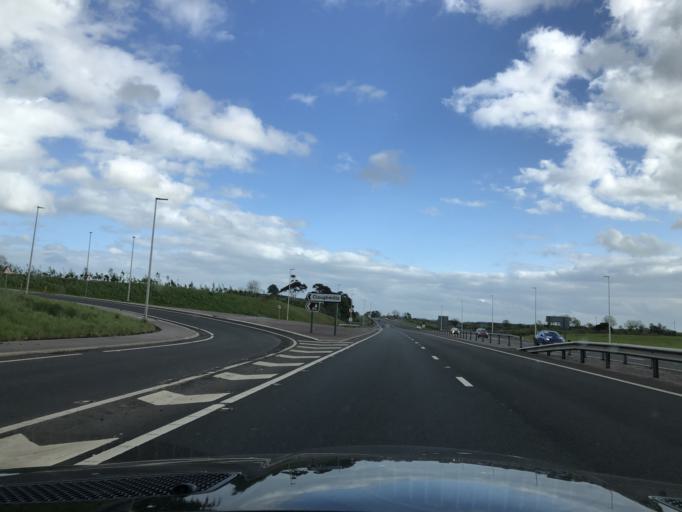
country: GB
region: Northern Ireland
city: Dunloy
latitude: 54.9846
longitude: -6.3485
